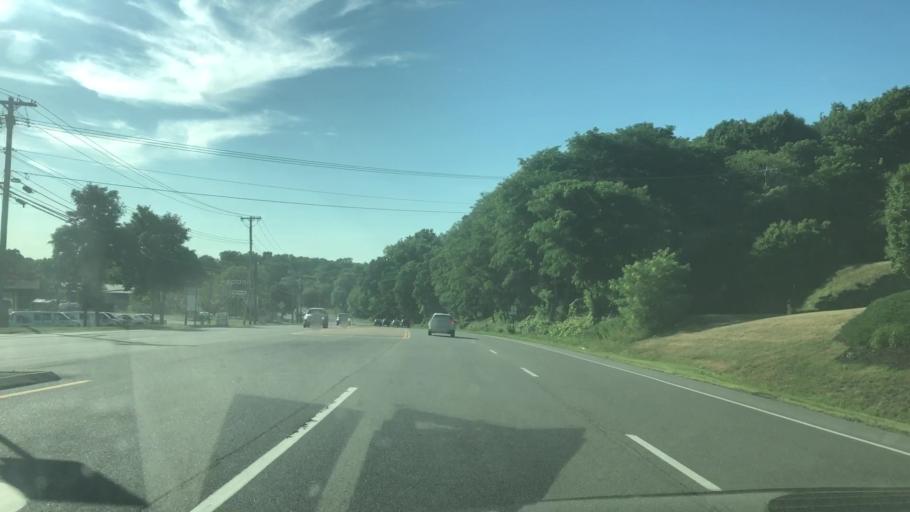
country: US
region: New York
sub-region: Ontario County
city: Victor
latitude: 43.0335
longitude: -77.4430
